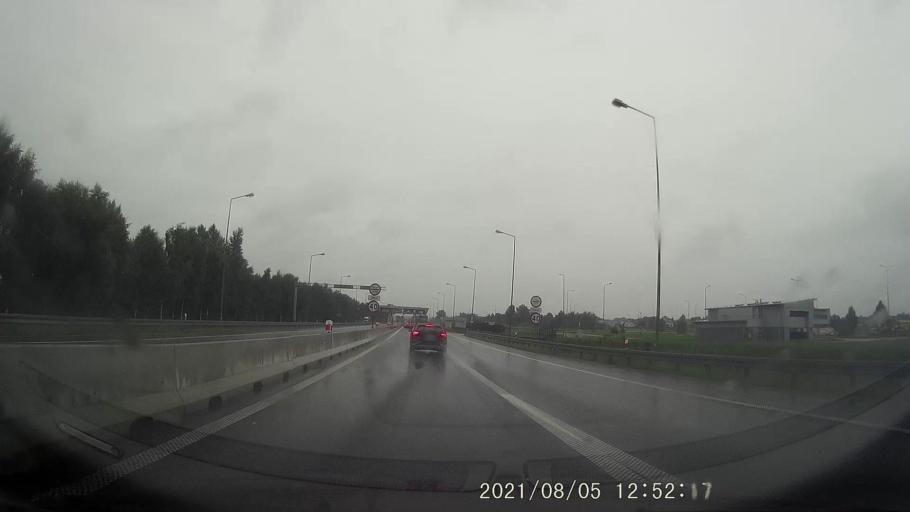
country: PL
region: Opole Voivodeship
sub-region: Powiat krapkowicki
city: Krapkowice
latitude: 50.4858
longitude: 17.9918
